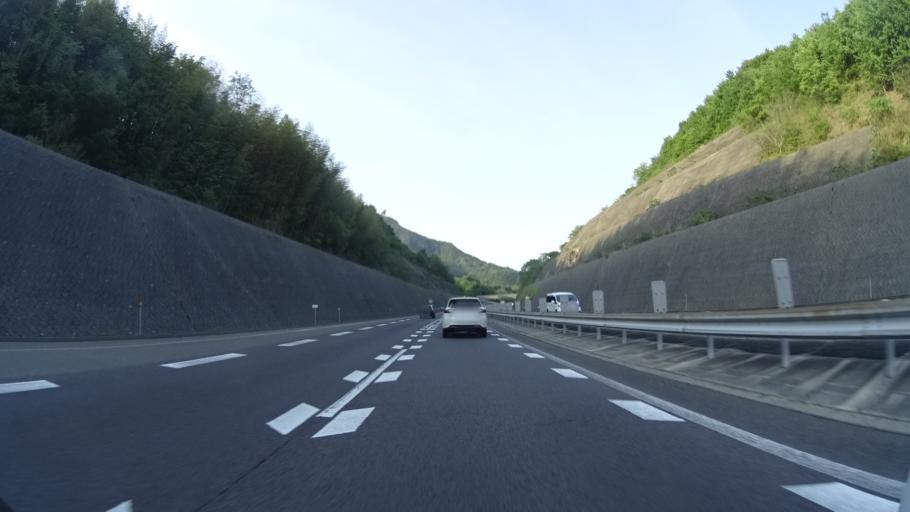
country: JP
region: Kagawa
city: Tadotsu
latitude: 34.2205
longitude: 133.7299
